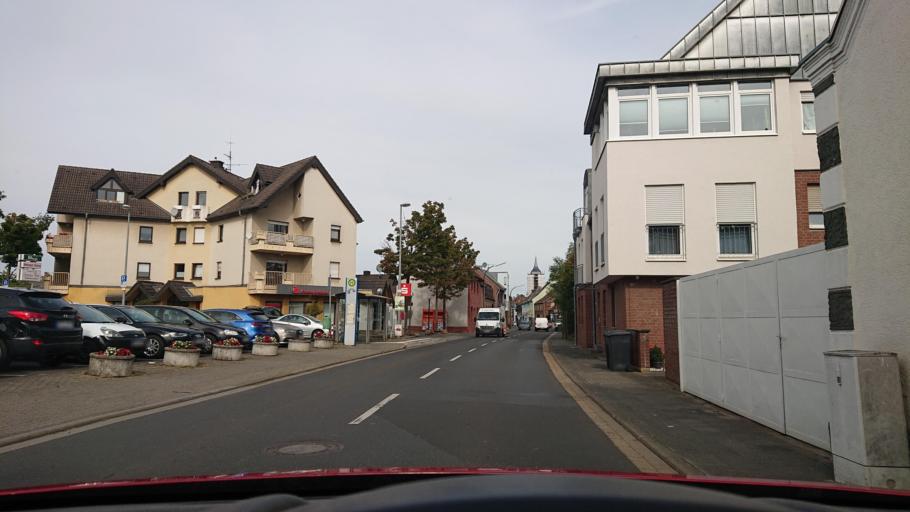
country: DE
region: North Rhine-Westphalia
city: Tuernich
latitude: 50.8363
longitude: 6.7432
